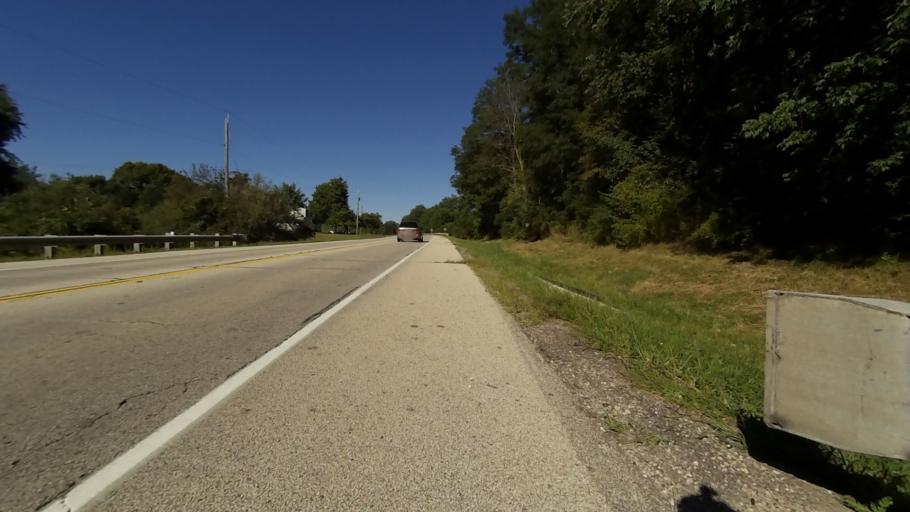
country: US
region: Ohio
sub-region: Portage County
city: Kent
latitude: 41.1356
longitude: -81.3882
